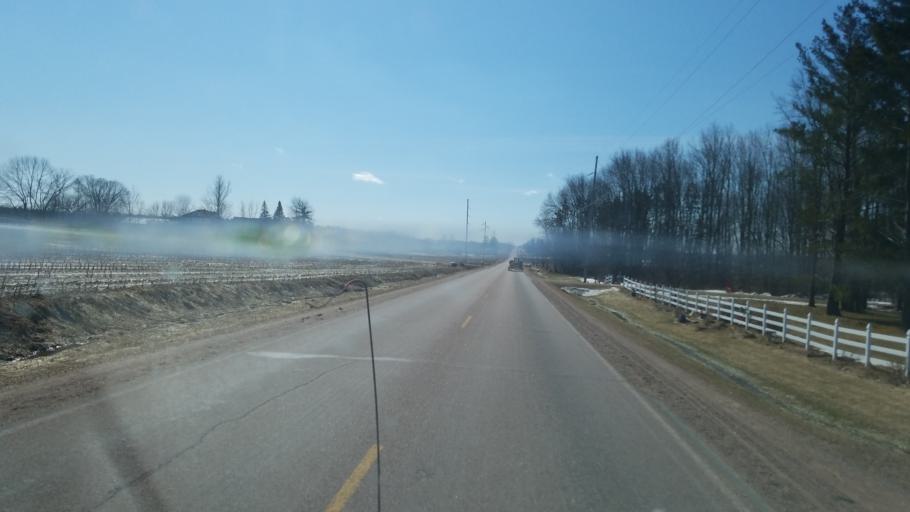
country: US
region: Wisconsin
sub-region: Clark County
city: Loyal
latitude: 44.5734
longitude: -90.3959
